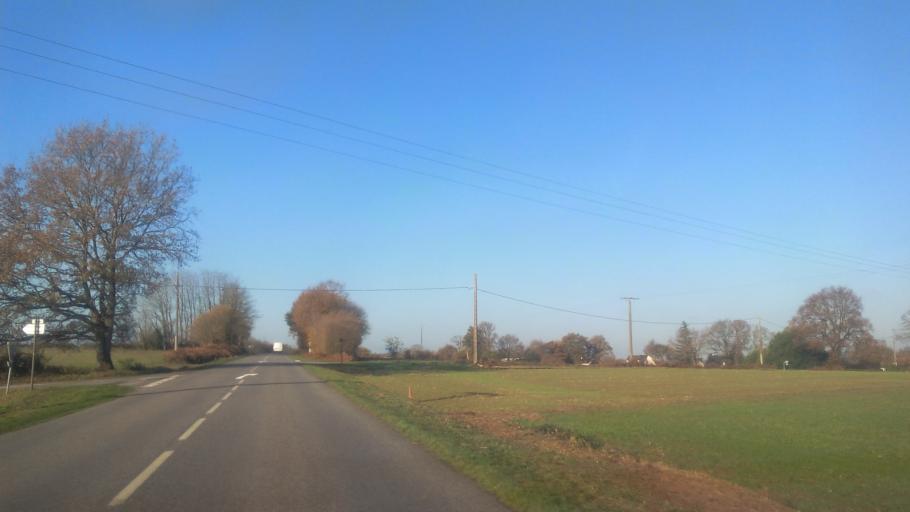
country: FR
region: Brittany
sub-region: Departement du Morbihan
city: Saint-Vincent-sur-Oust
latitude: 47.7117
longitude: -2.1752
